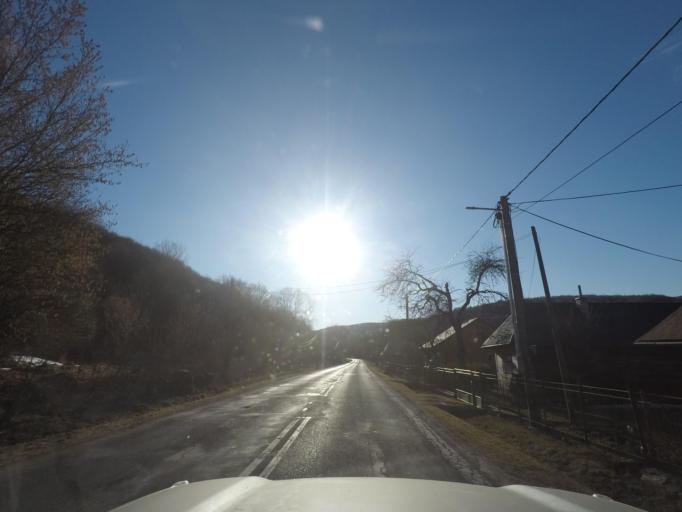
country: SK
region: Presovsky
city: Medzilaborce
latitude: 49.2802
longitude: 21.8189
